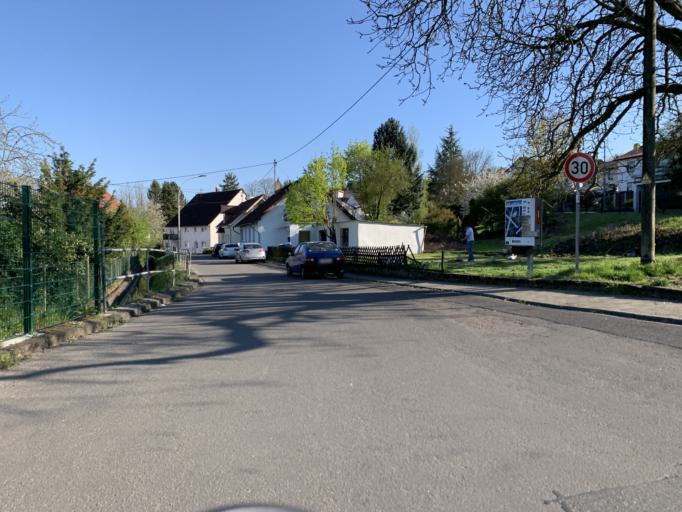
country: DE
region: Rheinland-Pfalz
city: Windesheim
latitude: 49.8908
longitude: 7.8388
